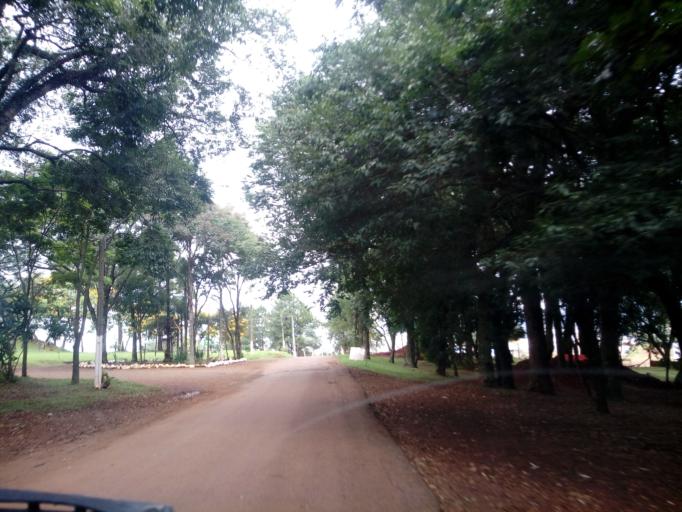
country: BR
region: Santa Catarina
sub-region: Chapeco
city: Chapeco
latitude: -27.0974
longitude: -52.6416
